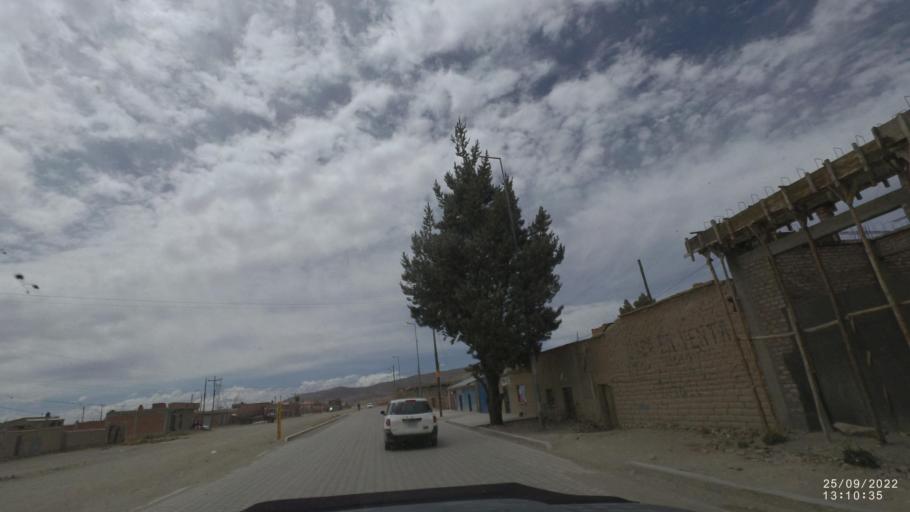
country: BO
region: Oruro
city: Oruro
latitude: -17.9709
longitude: -67.0485
